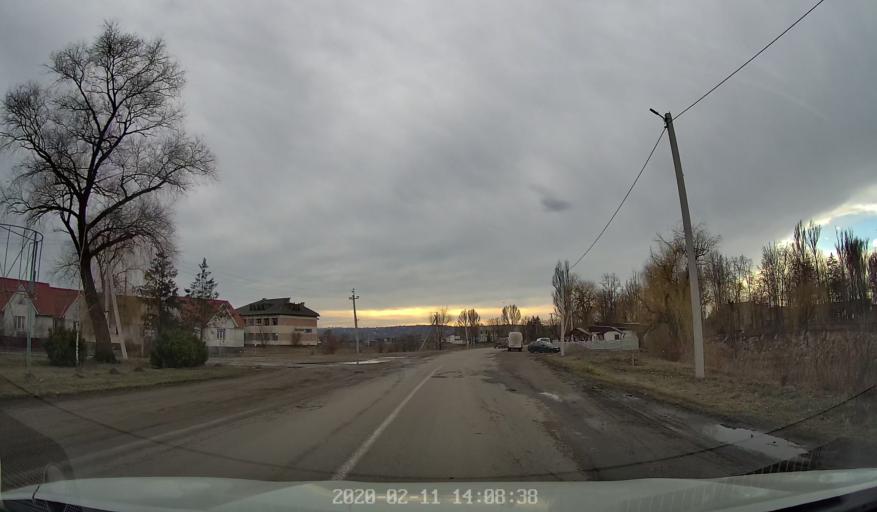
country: RO
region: Botosani
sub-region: Comuna Darabani
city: Bajura
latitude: 48.2353
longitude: 26.5459
